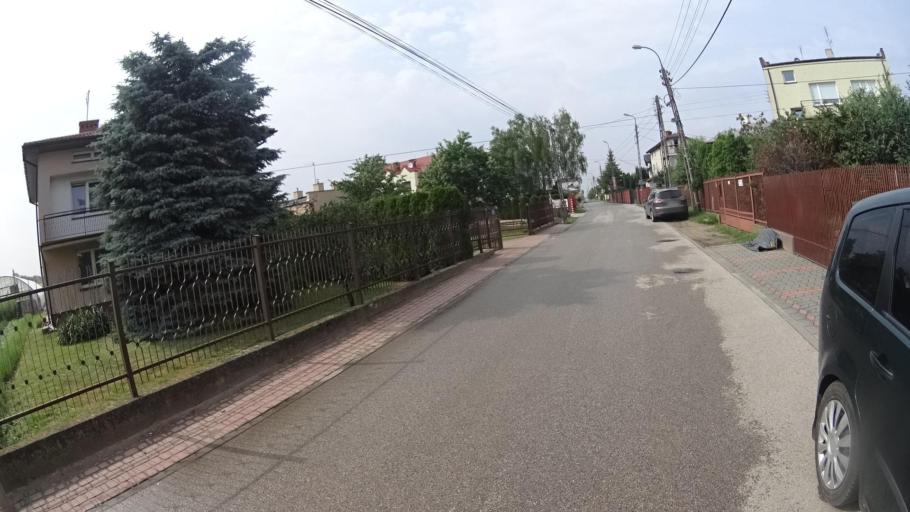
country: PL
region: Masovian Voivodeship
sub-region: Powiat pruszkowski
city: Raszyn
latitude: 52.1630
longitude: 20.9203
